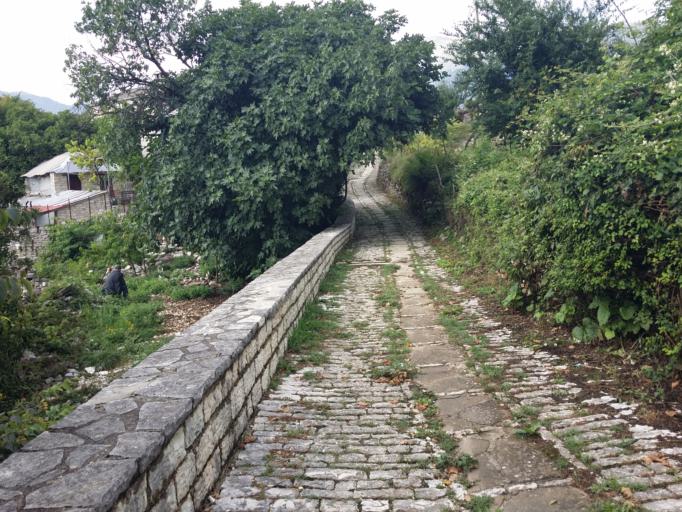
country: GR
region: Epirus
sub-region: Nomos Ioanninon
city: Kalpaki
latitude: 39.9520
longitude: 20.7068
